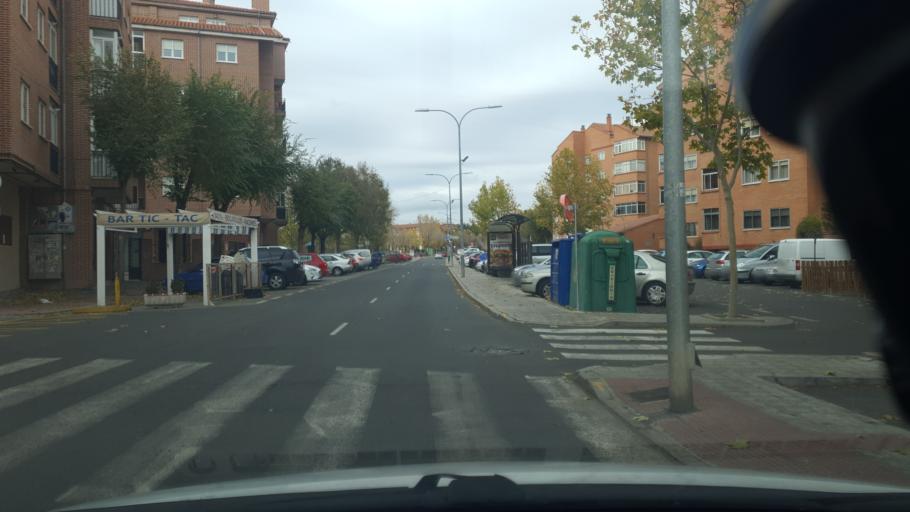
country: ES
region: Castille and Leon
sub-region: Provincia de Avila
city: Avila
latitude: 40.6466
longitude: -4.6843
